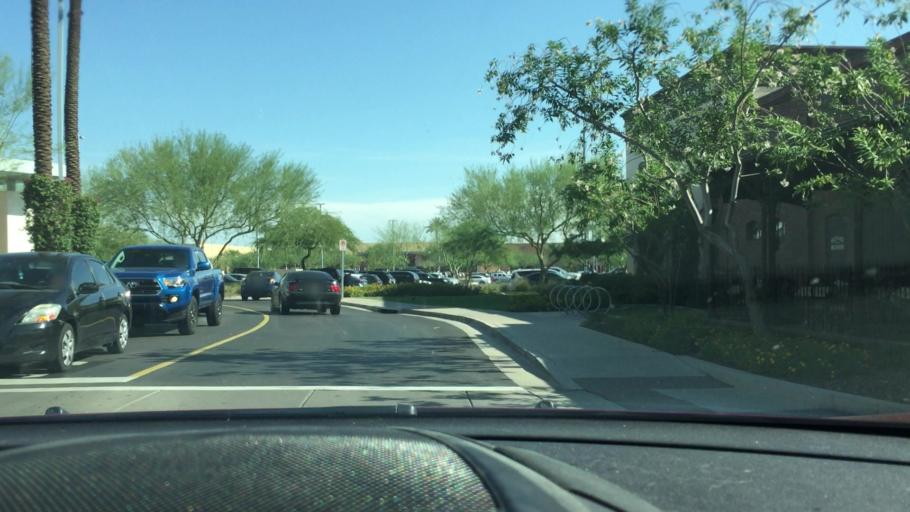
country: US
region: Arizona
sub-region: Maricopa County
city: Tempe
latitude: 33.4326
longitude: -111.9059
